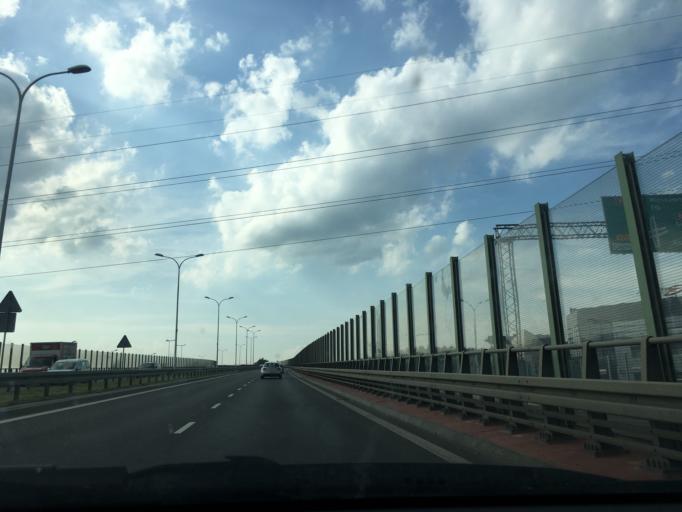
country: PL
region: Podlasie
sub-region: Bialystok
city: Bialystok
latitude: 53.1576
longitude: 23.1543
